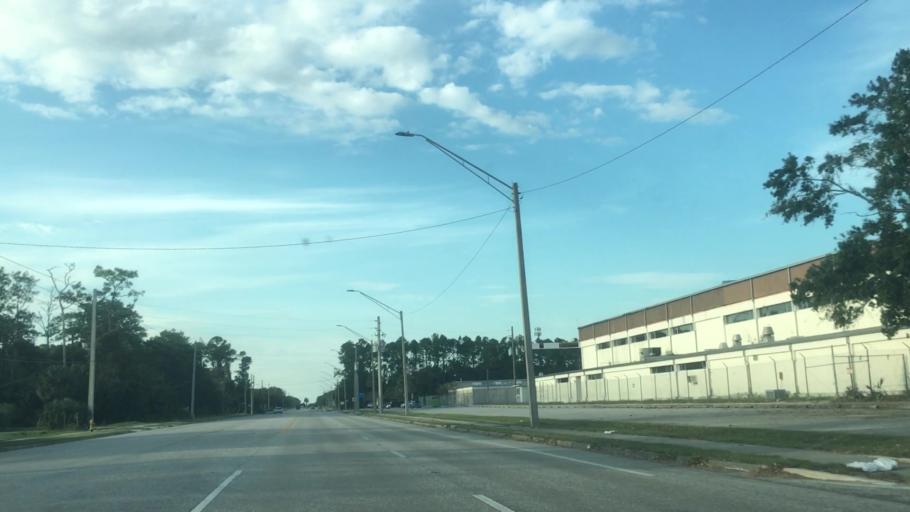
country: US
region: Florida
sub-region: Duval County
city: Atlantic Beach
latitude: 30.3300
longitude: -81.5232
